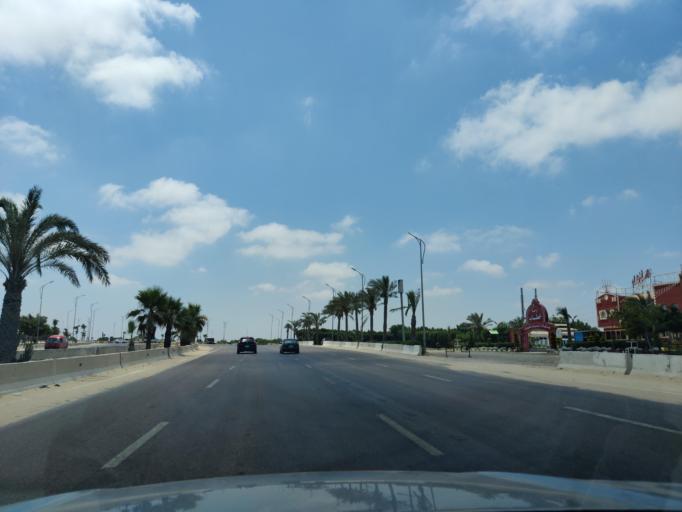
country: EG
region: Alexandria
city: Alexandria
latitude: 30.9776
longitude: 29.6602
